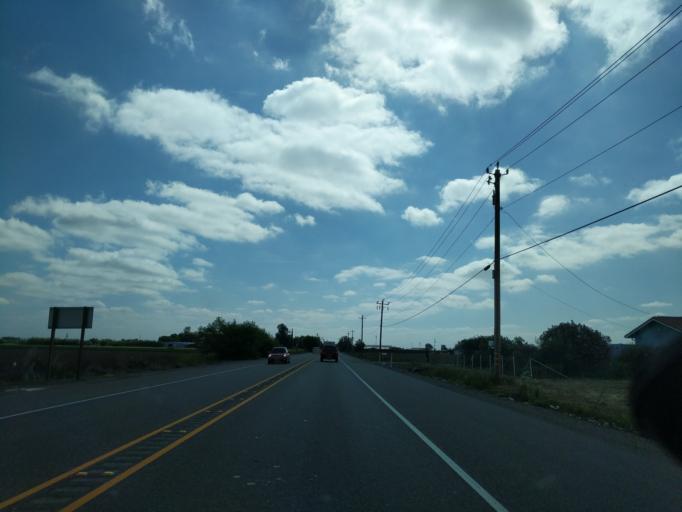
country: US
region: California
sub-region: Contra Costa County
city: Brentwood
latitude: 37.8968
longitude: -121.6750
